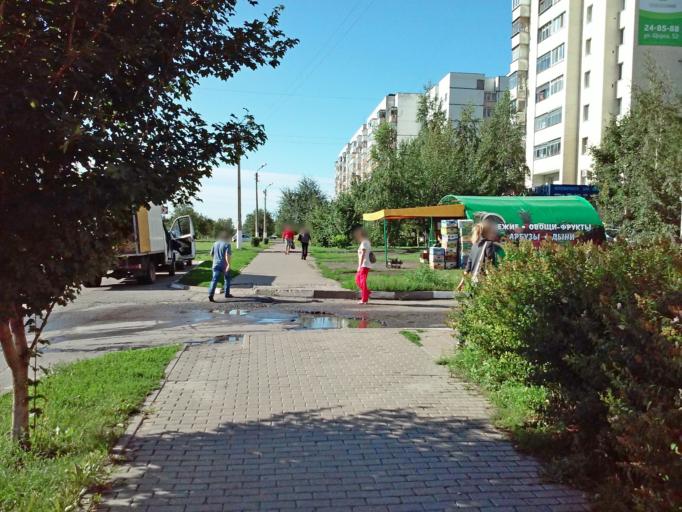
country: RU
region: Belgorod
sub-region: Belgorodskiy Rayon
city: Belgorod
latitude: 50.5580
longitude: 36.5715
